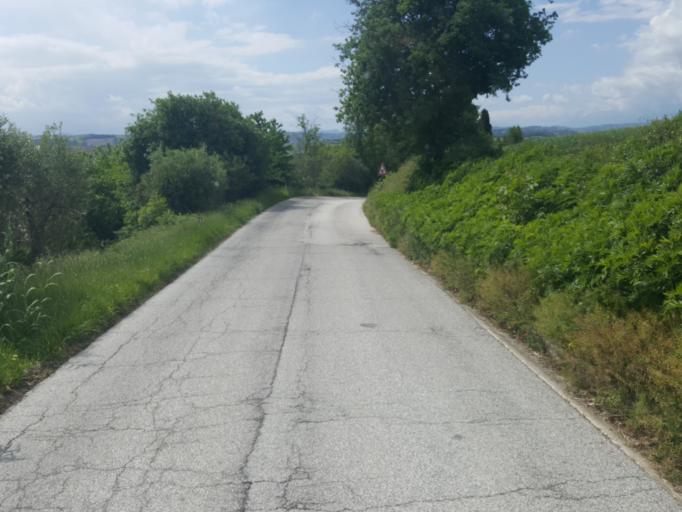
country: IT
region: The Marches
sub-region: Provincia di Macerata
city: Pollenza
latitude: 43.2564
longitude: 13.3688
